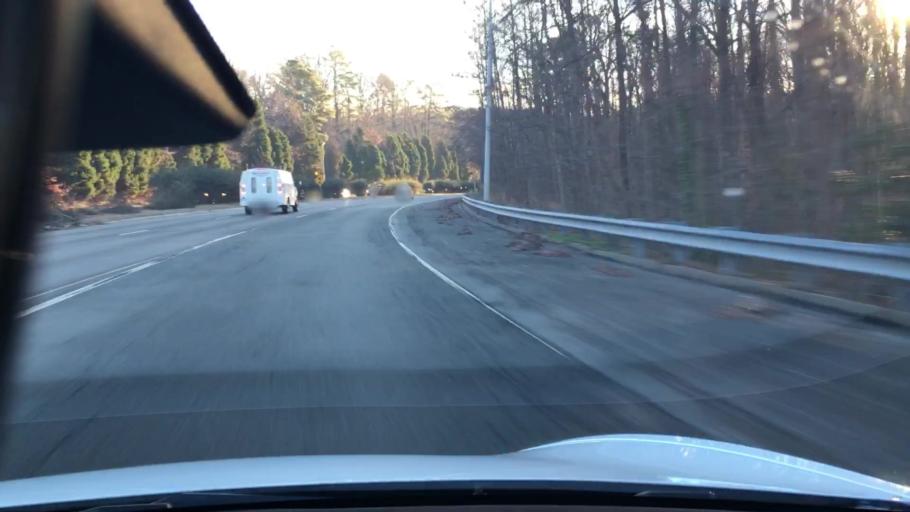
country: US
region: Virginia
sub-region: Chesterfield County
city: Bon Air
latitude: 37.5458
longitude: -77.5497
